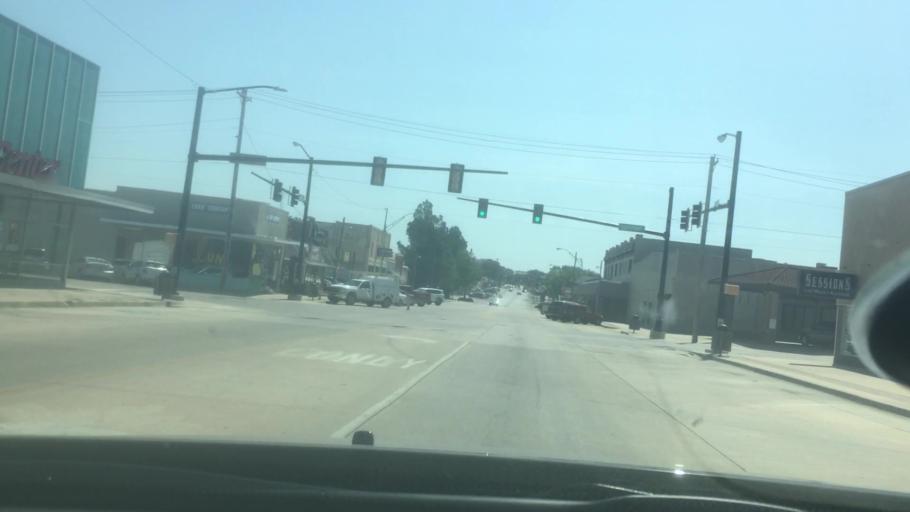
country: US
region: Oklahoma
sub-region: Pontotoc County
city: Ada
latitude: 34.7745
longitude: -96.6759
